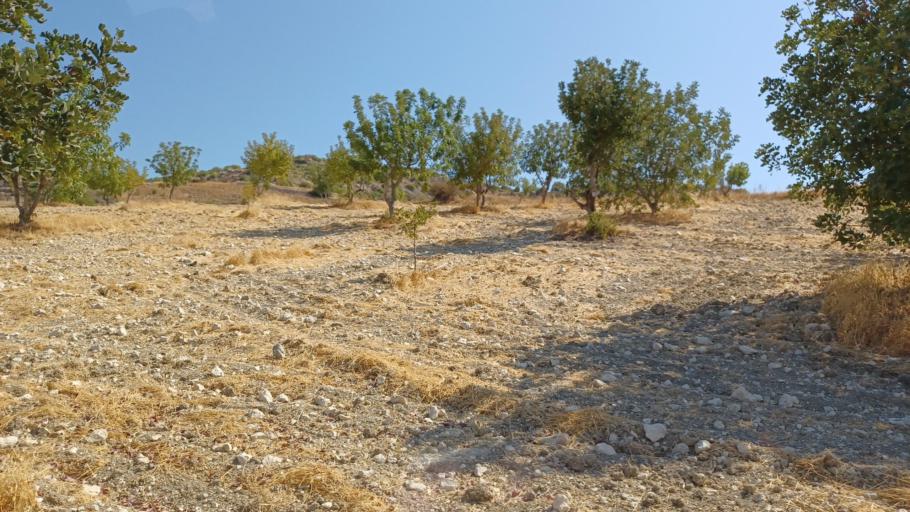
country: CY
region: Pafos
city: Polis
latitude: 34.9713
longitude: 32.4948
